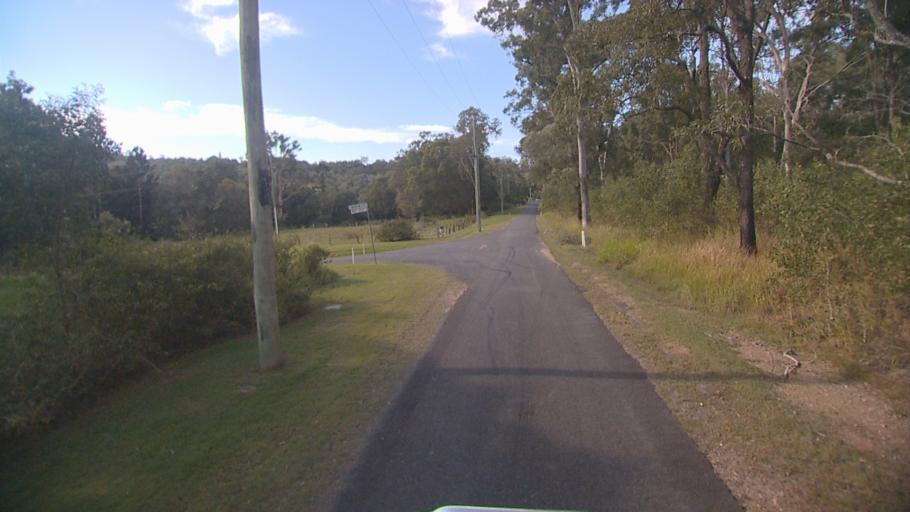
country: AU
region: Queensland
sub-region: Logan
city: Windaroo
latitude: -27.7760
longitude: 153.1757
